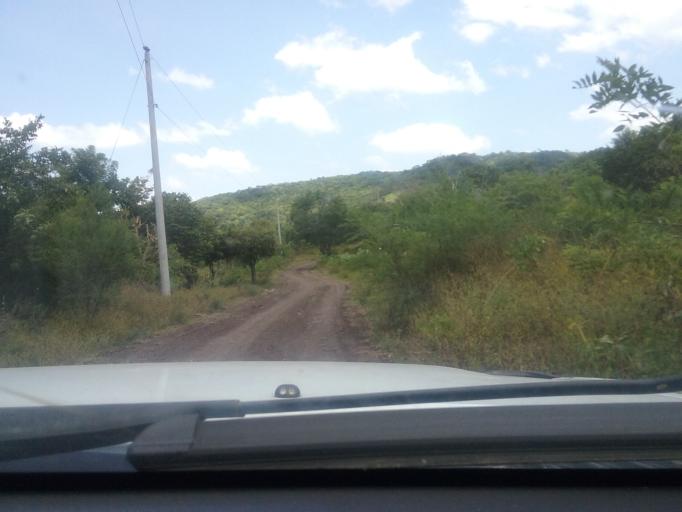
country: NI
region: Matagalpa
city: Terrabona
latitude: 12.6534
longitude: -86.0036
